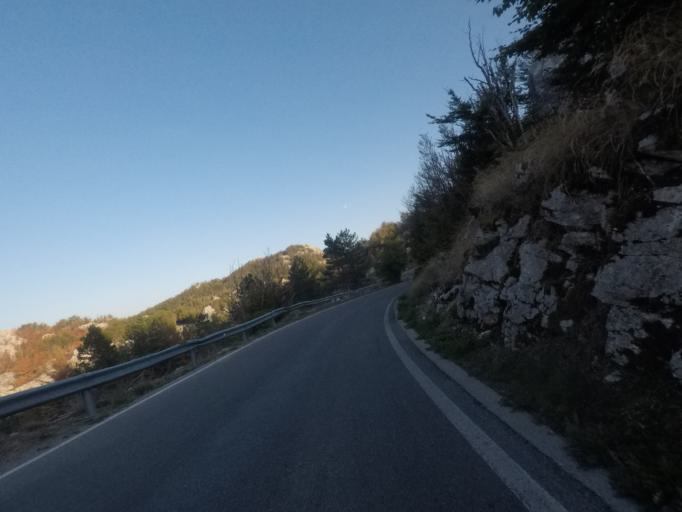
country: ME
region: Cetinje
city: Cetinje
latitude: 42.3805
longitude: 18.8464
